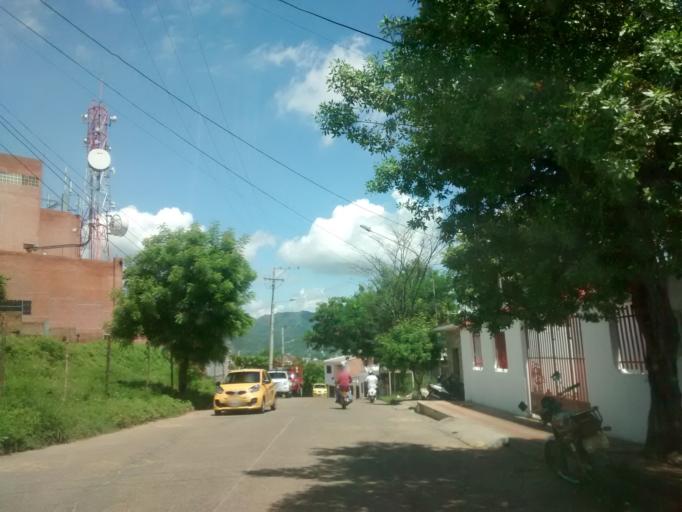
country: CO
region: Cundinamarca
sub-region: Girardot
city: Girardot City
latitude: 4.2967
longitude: -74.7984
